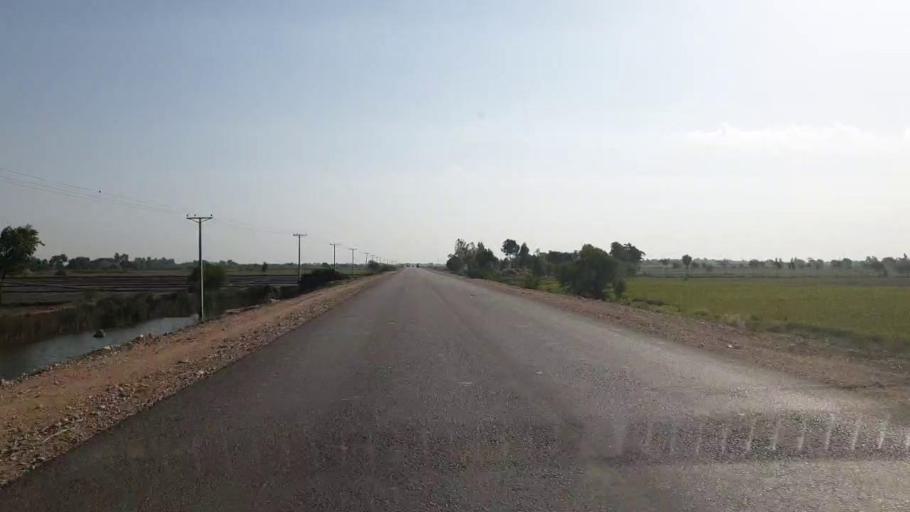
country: PK
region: Sindh
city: Tando Bago
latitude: 24.6571
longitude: 69.0096
